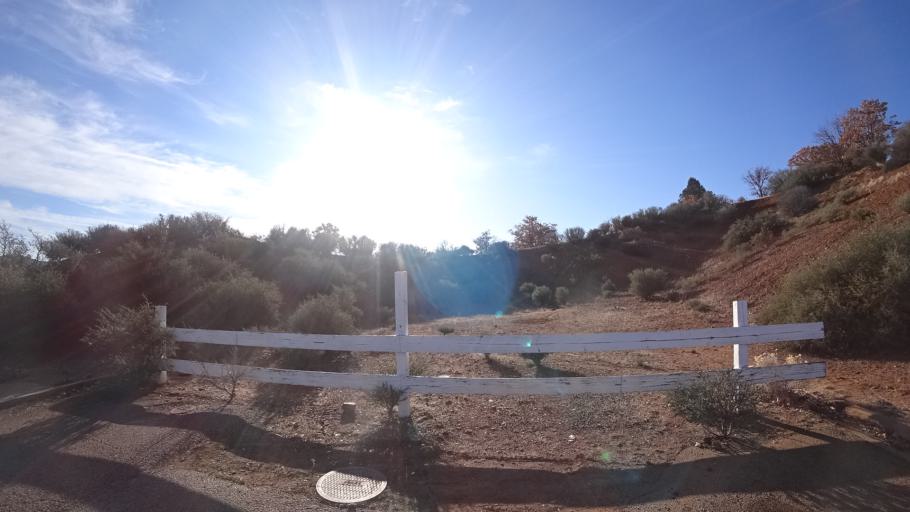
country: US
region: California
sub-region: Siskiyou County
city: Yreka
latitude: 41.7077
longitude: -122.6231
